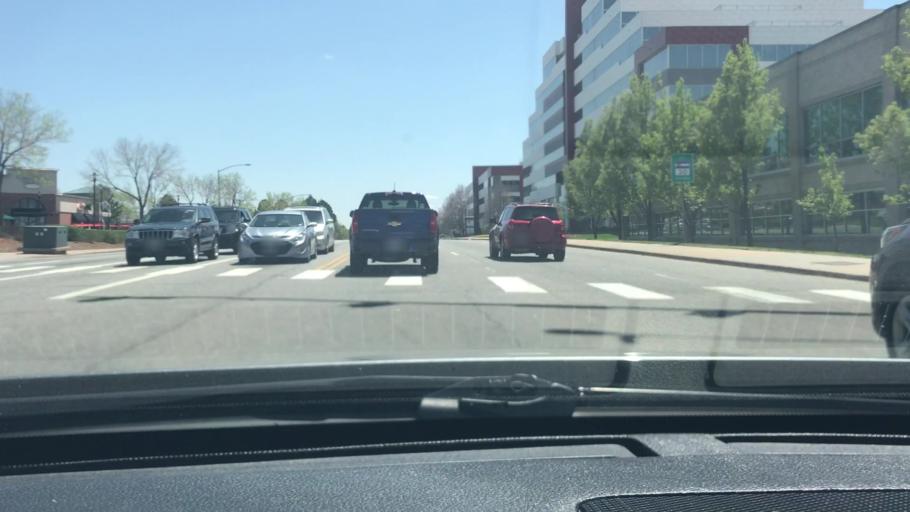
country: US
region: Colorado
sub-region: Adams County
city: Aurora
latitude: 39.6747
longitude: -104.8708
